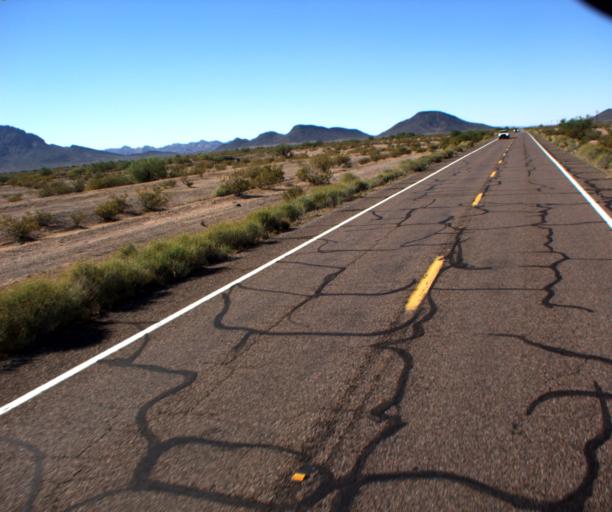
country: US
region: Arizona
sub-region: Maricopa County
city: Gila Bend
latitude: 32.7993
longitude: -112.8000
